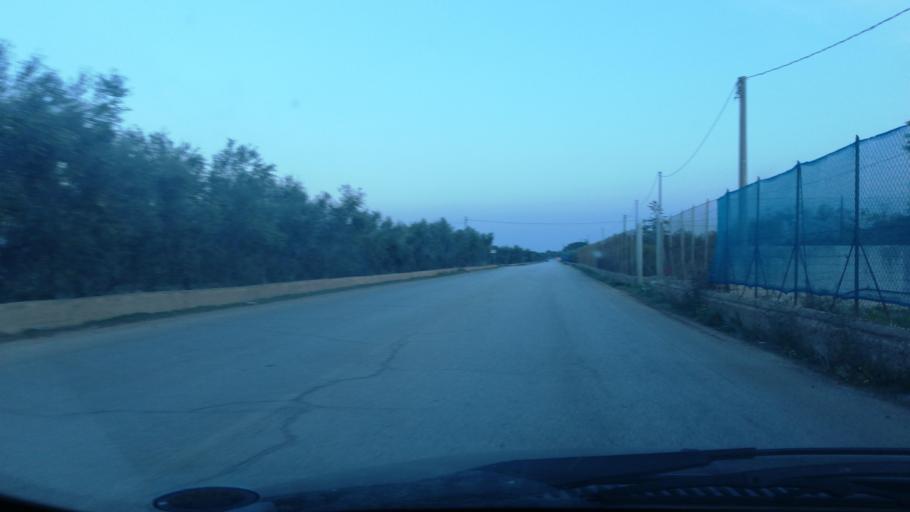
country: IT
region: Apulia
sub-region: Provincia di Bari
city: Bitonto
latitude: 41.1313
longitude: 16.7065
